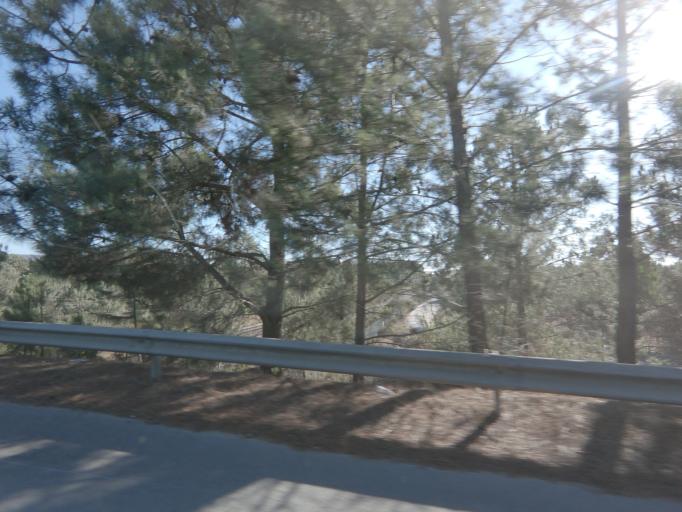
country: PT
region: Setubal
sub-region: Palmela
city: Pinhal Novo
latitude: 38.6169
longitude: -8.9535
